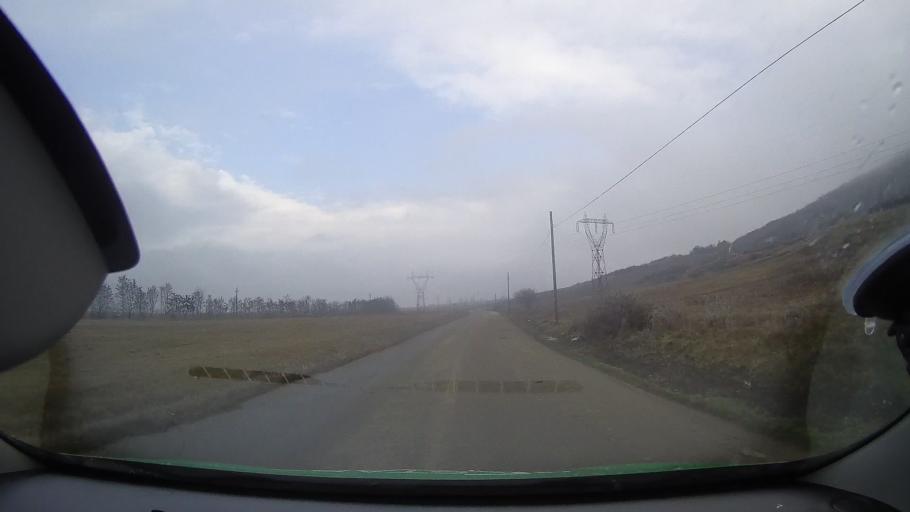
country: RO
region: Alba
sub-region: Comuna Noslac
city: Noslac
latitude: 46.4103
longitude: 23.9570
